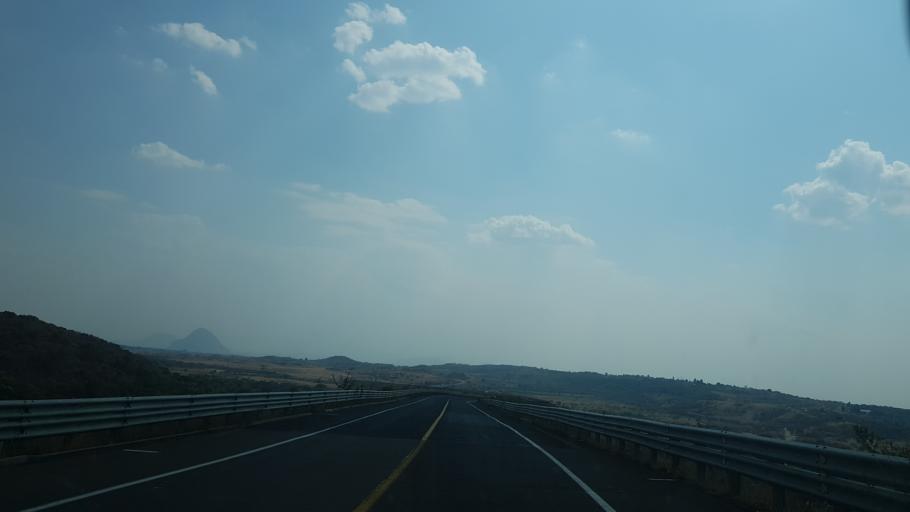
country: MX
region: Puebla
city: San Juan Amecac
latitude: 18.8215
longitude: -98.6901
